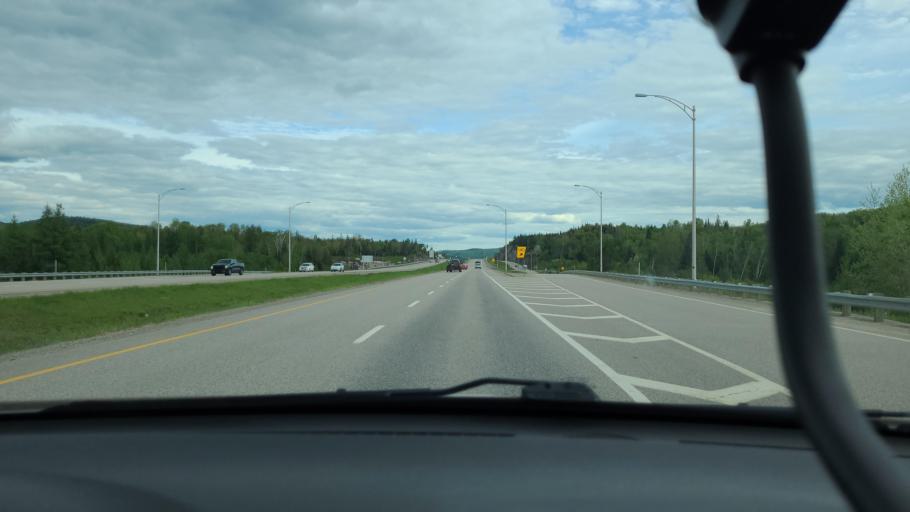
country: CA
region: Quebec
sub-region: Laurentides
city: Labelle
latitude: 46.2607
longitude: -74.7274
